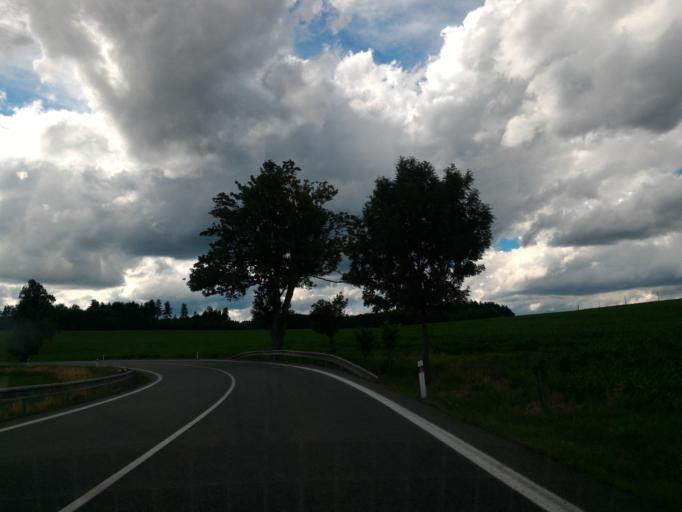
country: CZ
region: Vysocina
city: Bohdalov
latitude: 49.4771
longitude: 15.8261
